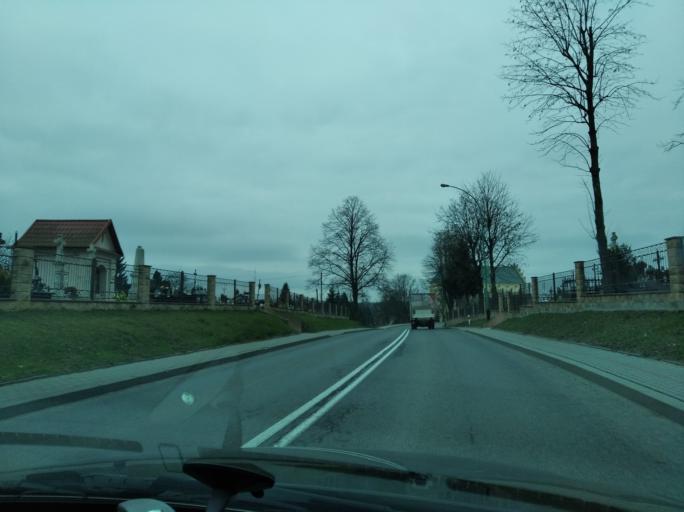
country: PL
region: Subcarpathian Voivodeship
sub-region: Powiat lancucki
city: Zolynia
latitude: 50.1692
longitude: 22.3104
